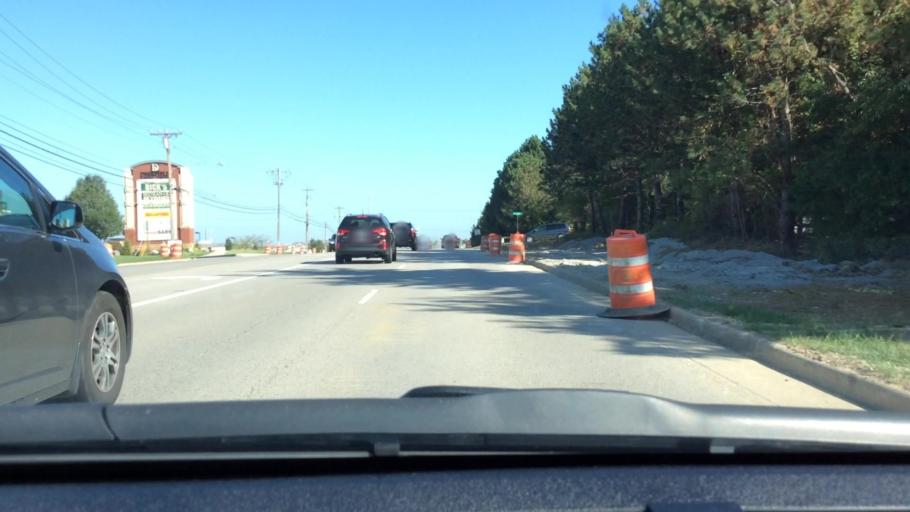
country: US
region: Ohio
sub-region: Warren County
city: Landen
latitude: 39.3049
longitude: -84.3143
